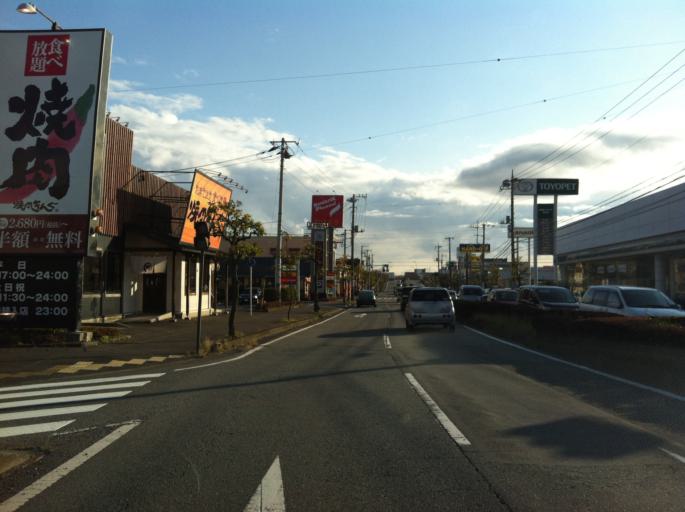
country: JP
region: Shizuoka
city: Fuji
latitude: 35.1645
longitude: 138.6697
